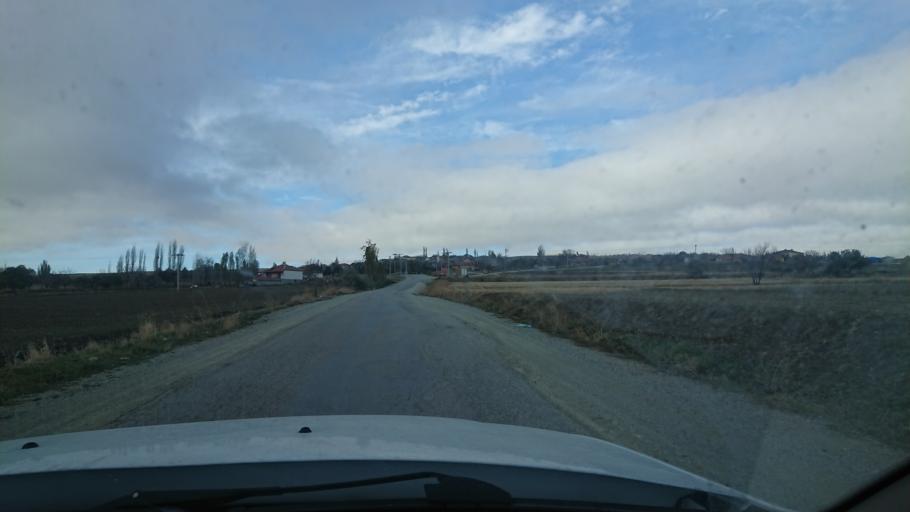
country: TR
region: Aksaray
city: Ortakoy
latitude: 38.7552
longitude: 34.0171
